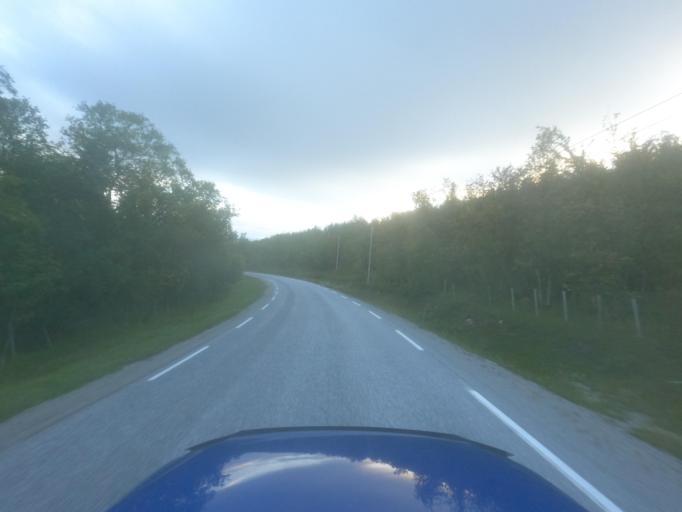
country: NO
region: Finnmark Fylke
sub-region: Porsanger
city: Lakselv
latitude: 70.3674
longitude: 25.0771
